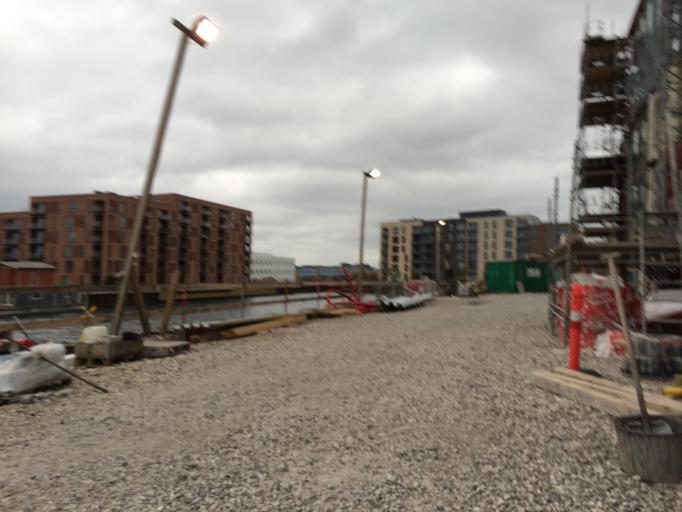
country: DK
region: Capital Region
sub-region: Kobenhavn
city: Copenhagen
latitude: 55.6545
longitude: 12.5522
